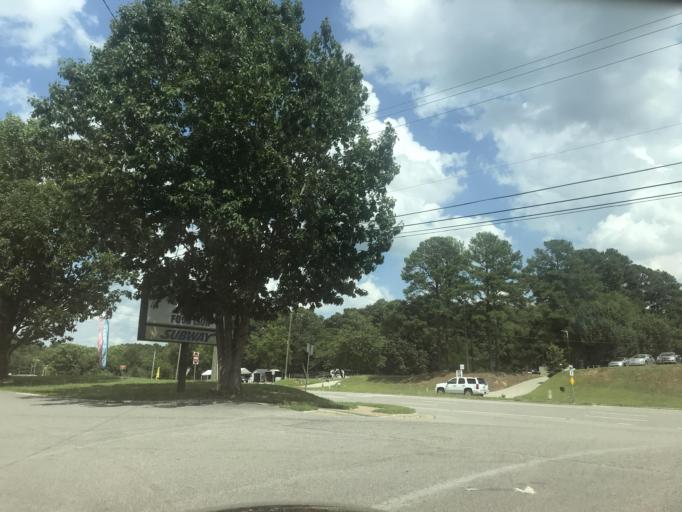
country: US
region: North Carolina
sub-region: Wake County
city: Knightdale
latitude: 35.8541
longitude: -78.5578
